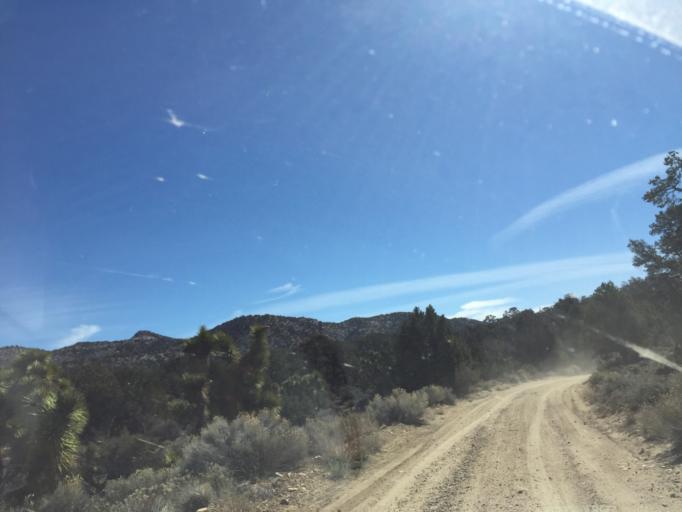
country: US
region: California
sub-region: San Bernardino County
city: Big Bear City
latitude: 34.2472
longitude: -116.7115
